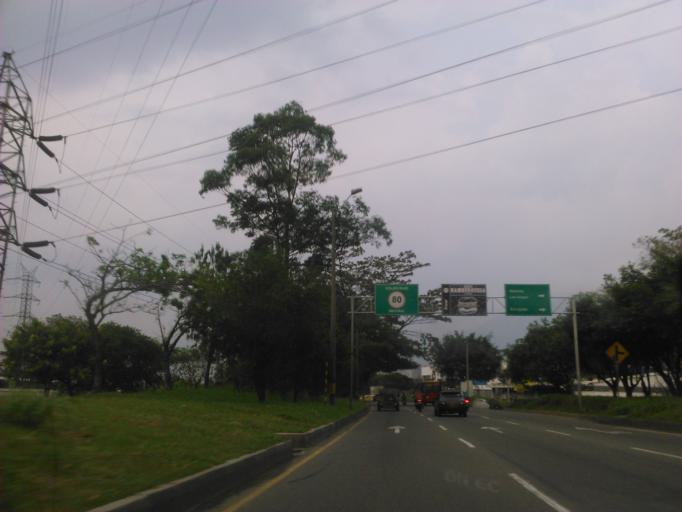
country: CO
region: Antioquia
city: Envigado
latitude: 6.1764
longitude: -75.5940
